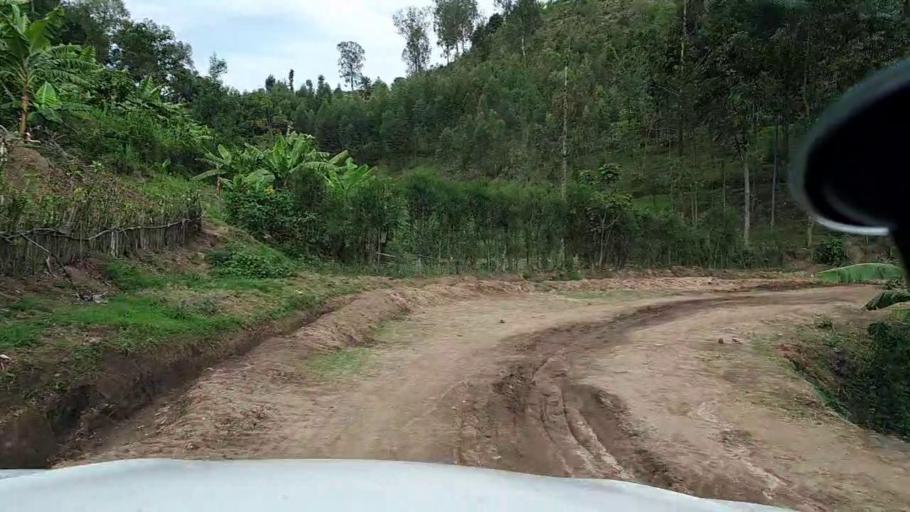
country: RW
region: Southern Province
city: Gitarama
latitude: -2.1276
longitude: 29.6600
